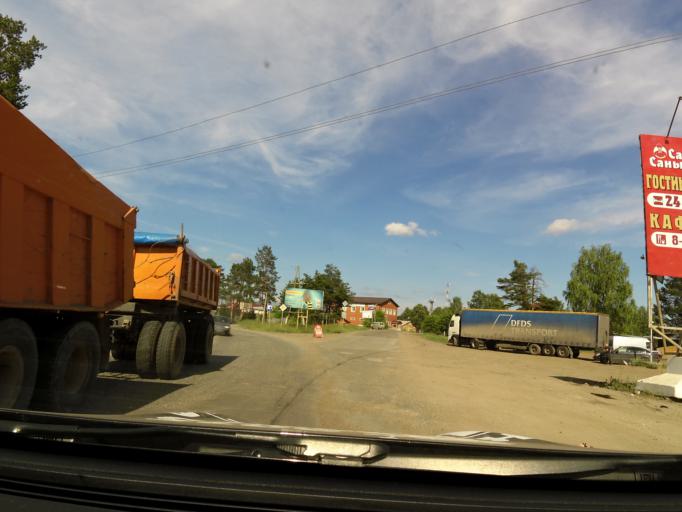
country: RU
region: Kirov
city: Belaya Kholunitsa
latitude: 58.8481
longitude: 50.8259
